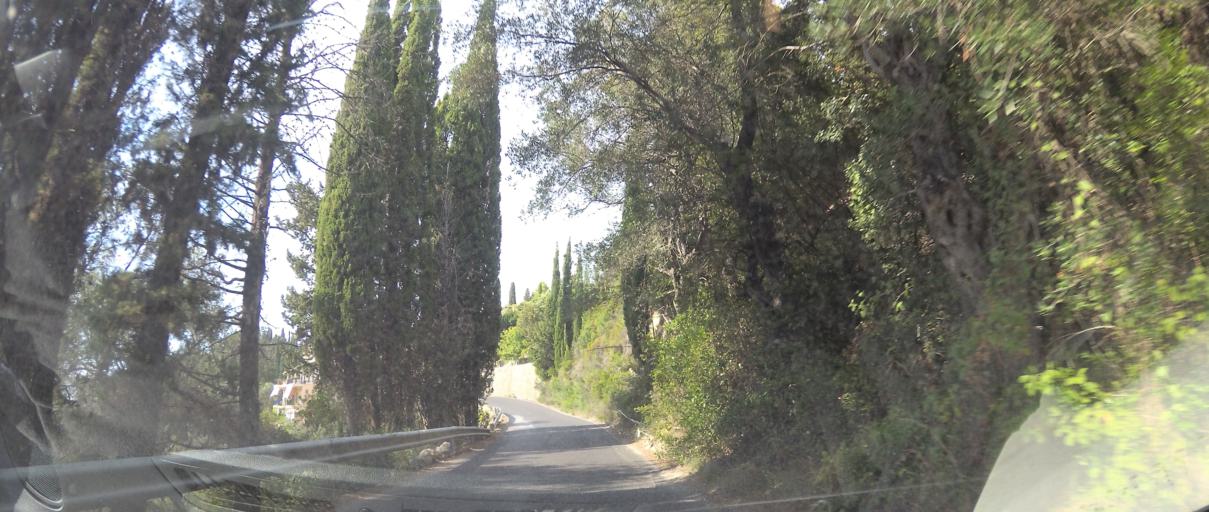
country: GR
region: Ionian Islands
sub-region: Nomos Kerkyras
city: Kynopiastes
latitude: 39.5516
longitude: 19.8630
